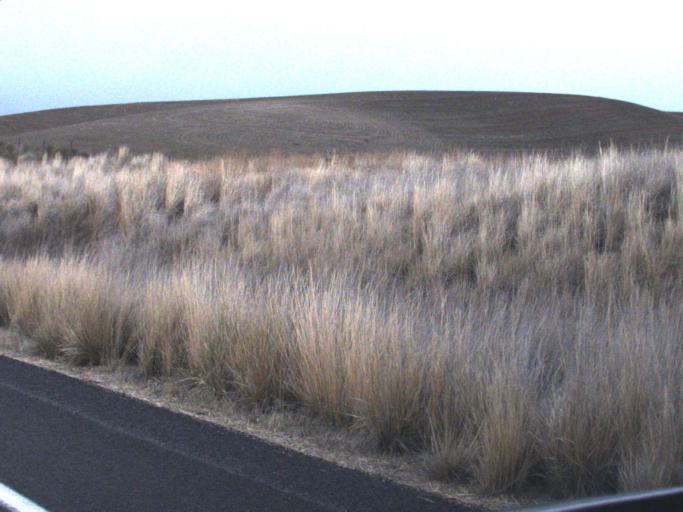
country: US
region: Washington
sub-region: Whitman County
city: Colfax
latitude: 46.8133
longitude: -117.5932
